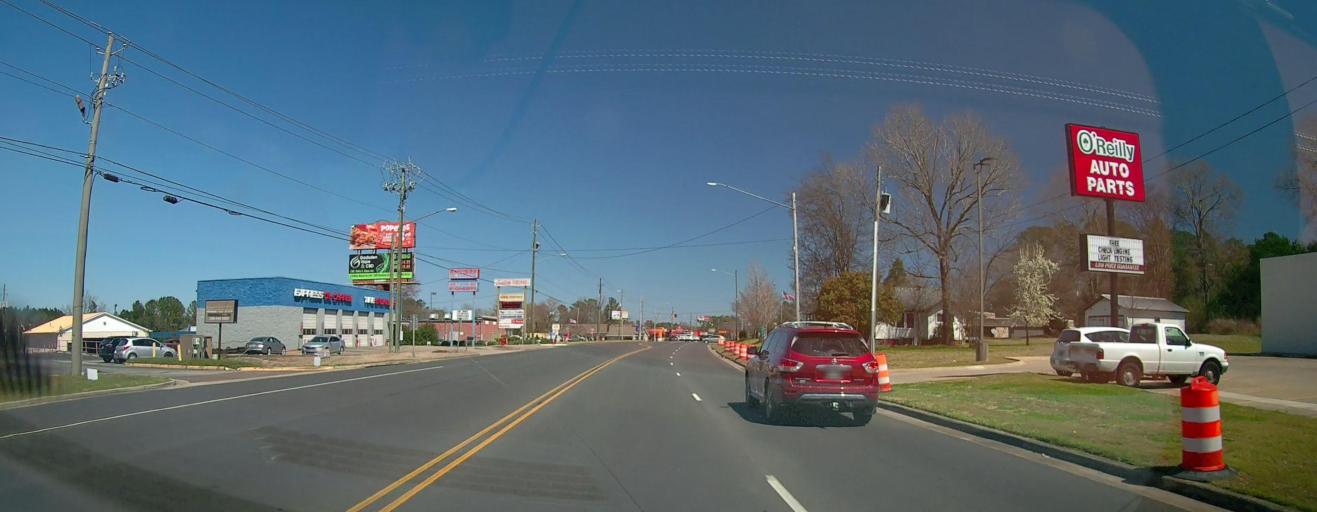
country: US
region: Alabama
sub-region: Etowah County
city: Rainbow City
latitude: 33.9557
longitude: -86.0405
